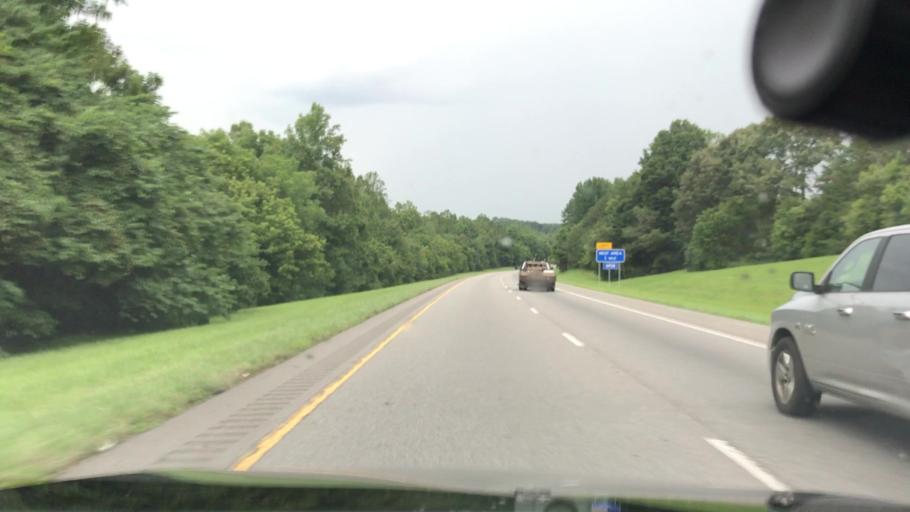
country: US
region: North Carolina
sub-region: Iredell County
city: Statesville
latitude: 35.8822
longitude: -80.8660
